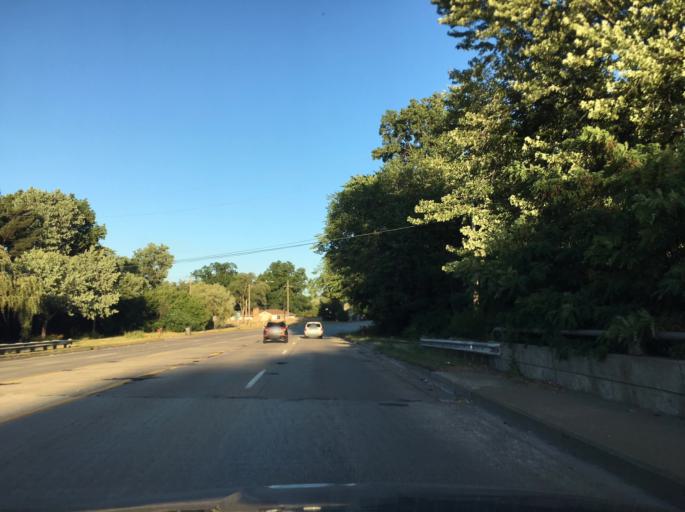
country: US
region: Michigan
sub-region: Macomb County
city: Fraser
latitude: 42.5685
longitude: -82.9693
